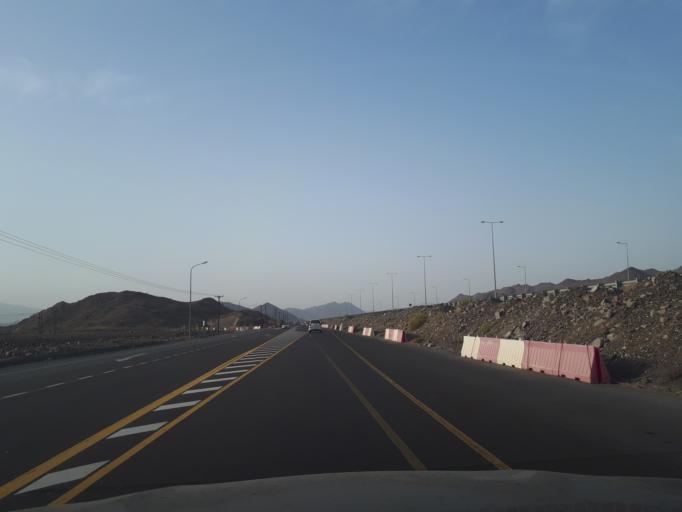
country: OM
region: Muhafazat ad Dakhiliyah
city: Sufalat Sama'il
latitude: 23.2816
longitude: 58.1076
